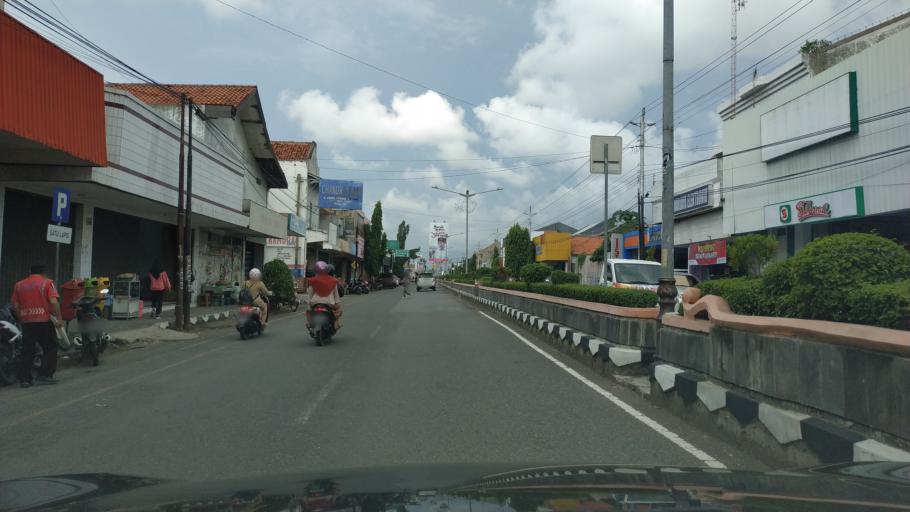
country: ID
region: Central Java
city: Pemalang
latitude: -6.8900
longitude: 109.3848
